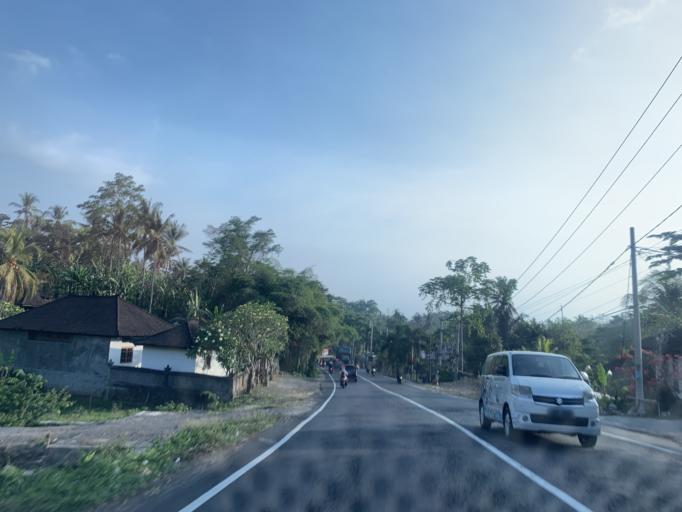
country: ID
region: Bali
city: Bajera
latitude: -8.5004
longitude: 115.0238
